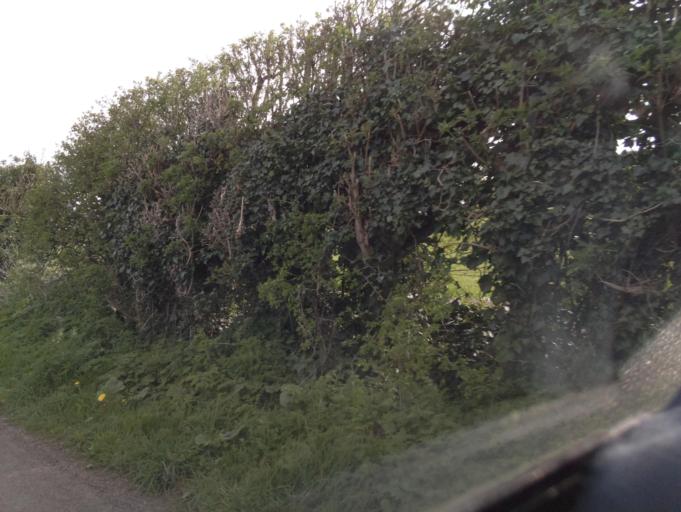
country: GB
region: England
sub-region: Somerset
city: Milborne Port
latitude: 50.9757
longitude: -2.4945
